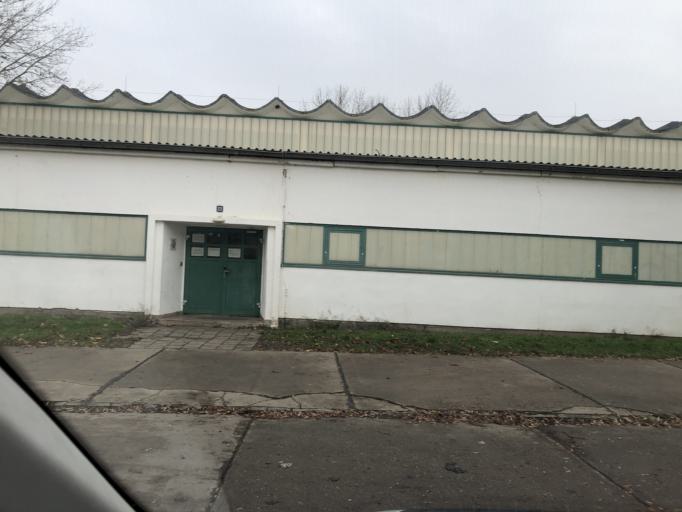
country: DE
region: Saxony-Anhalt
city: Halle Neustadt
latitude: 51.4682
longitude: 11.9281
